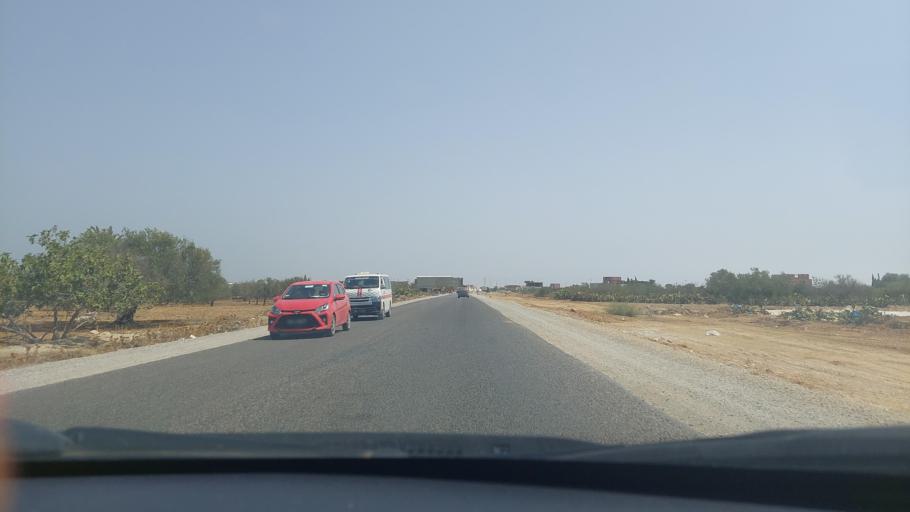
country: TN
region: Al Munastir
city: Qasr Hallal
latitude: 35.6048
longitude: 10.8847
